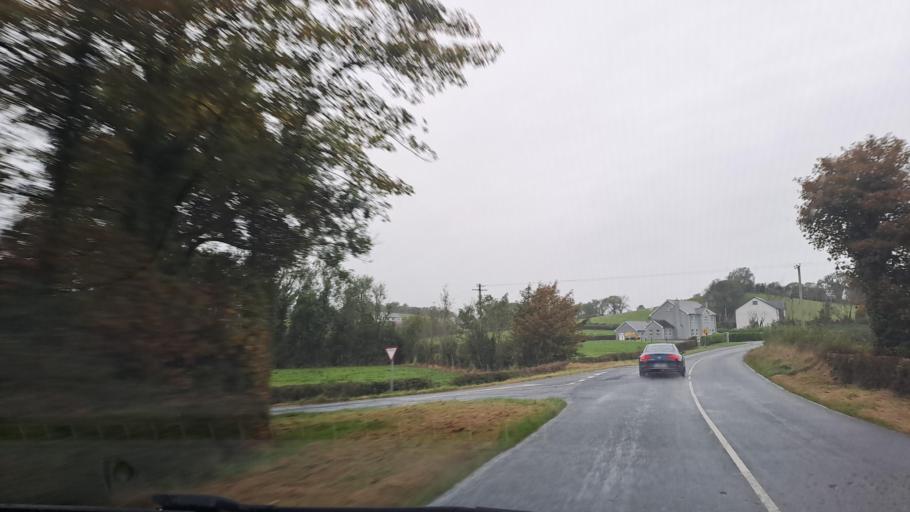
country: IE
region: Ulster
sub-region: County Monaghan
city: Monaghan
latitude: 54.2178
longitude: -6.9153
